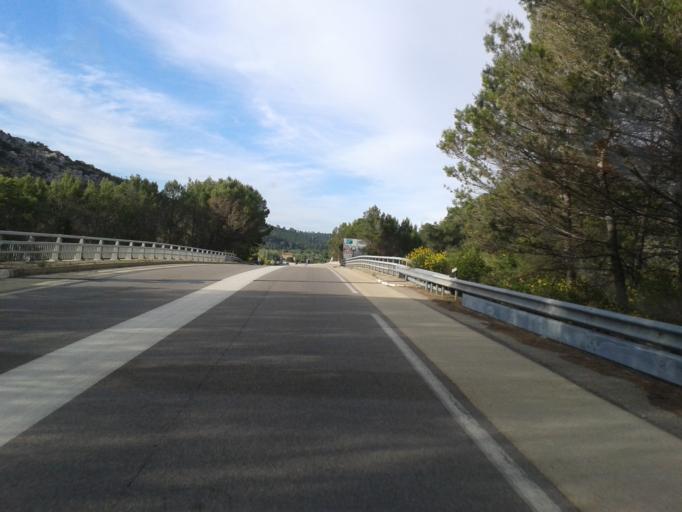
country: FR
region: Provence-Alpes-Cote d'Azur
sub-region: Departement du Vaucluse
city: Beaumont-de-Pertuis
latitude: 43.6868
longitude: 5.6655
